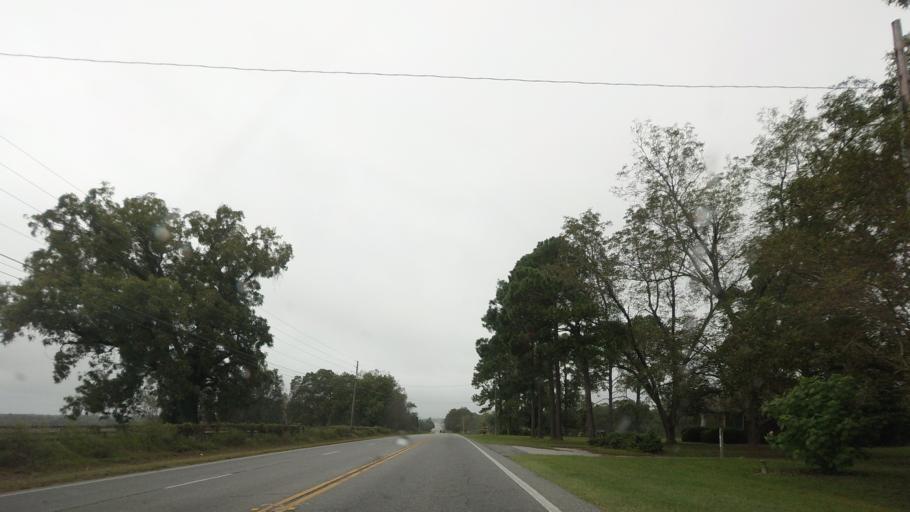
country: US
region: Georgia
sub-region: Ben Hill County
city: Fitzgerald
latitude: 31.6833
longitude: -83.2382
